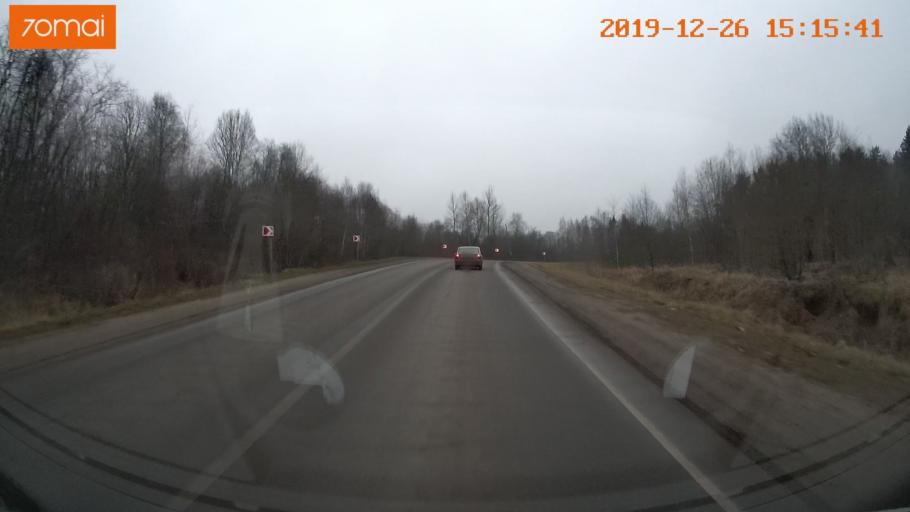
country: RU
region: Jaroslavl
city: Rybinsk
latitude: 58.0942
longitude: 38.8744
